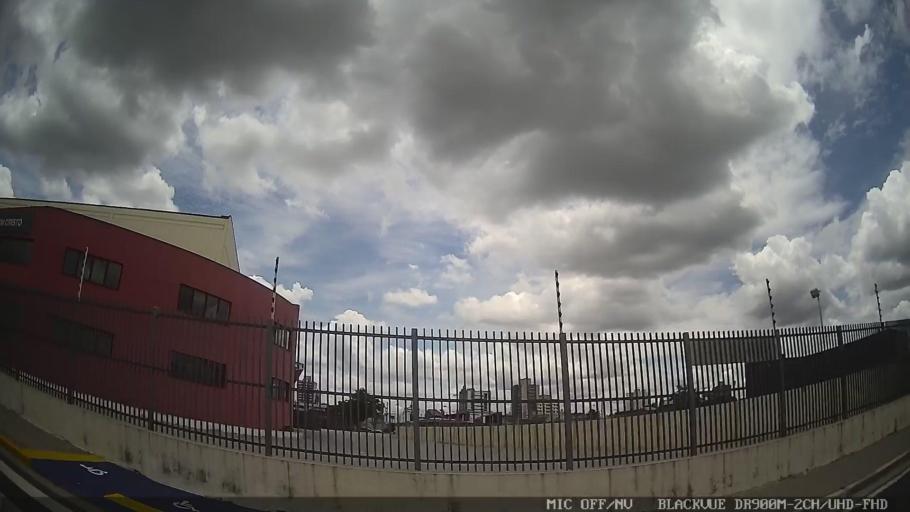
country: BR
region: Sao Paulo
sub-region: Suzano
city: Suzano
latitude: -23.5473
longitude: -46.3039
